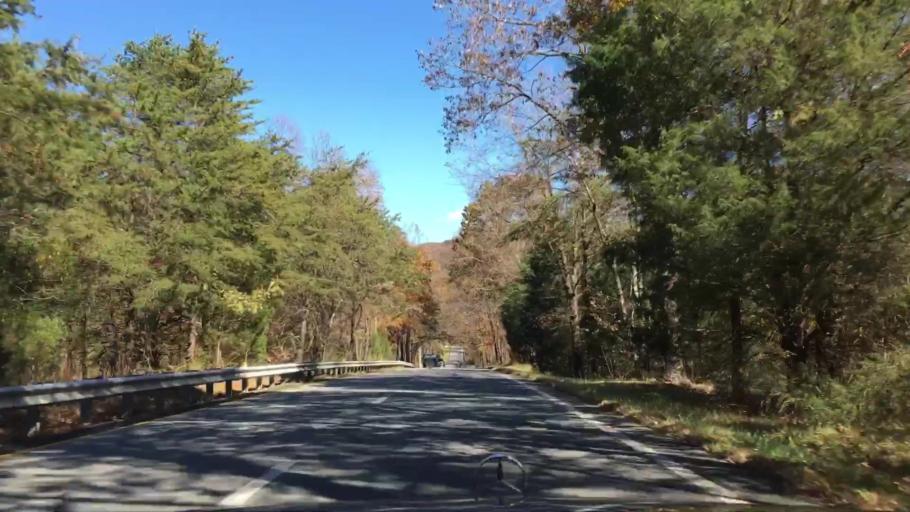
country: US
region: Virginia
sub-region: Nelson County
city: Nellysford
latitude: 37.8664
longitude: -78.7296
